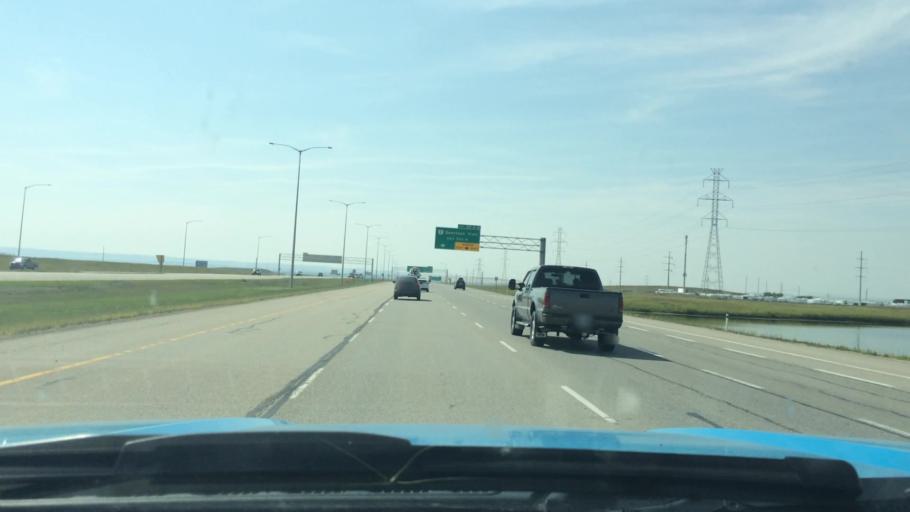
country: CA
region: Alberta
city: Airdrie
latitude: 51.1758
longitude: -113.9744
